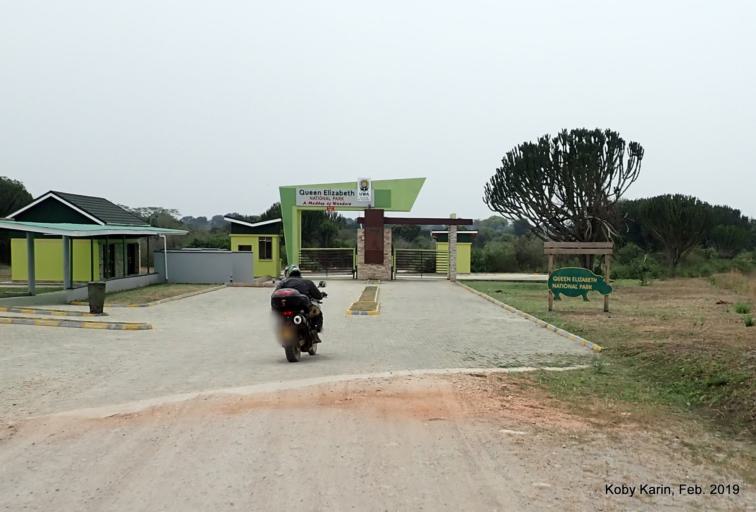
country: UG
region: Western Region
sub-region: Rubirizi District
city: Rubirizi
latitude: -0.1350
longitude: 29.9281
